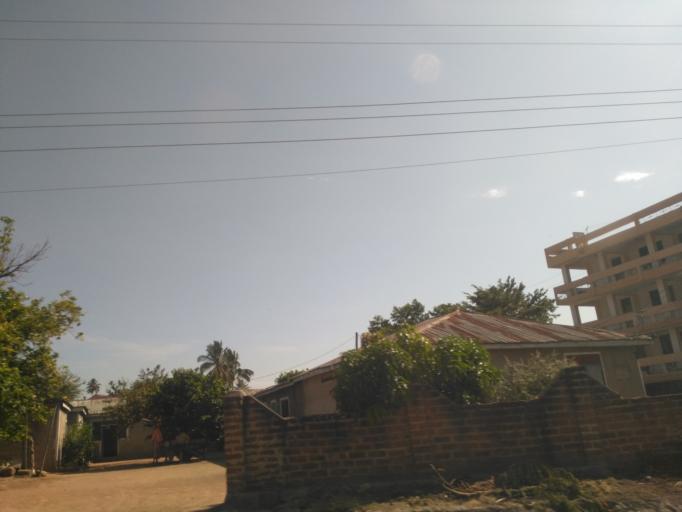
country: TZ
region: Mwanza
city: Mwanza
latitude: -2.5008
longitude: 32.8971
